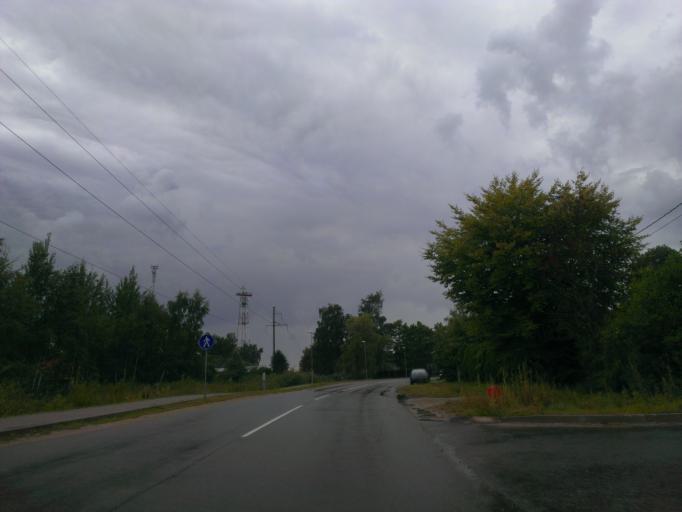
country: LV
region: Kegums
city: Kegums
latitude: 56.7490
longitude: 24.7300
